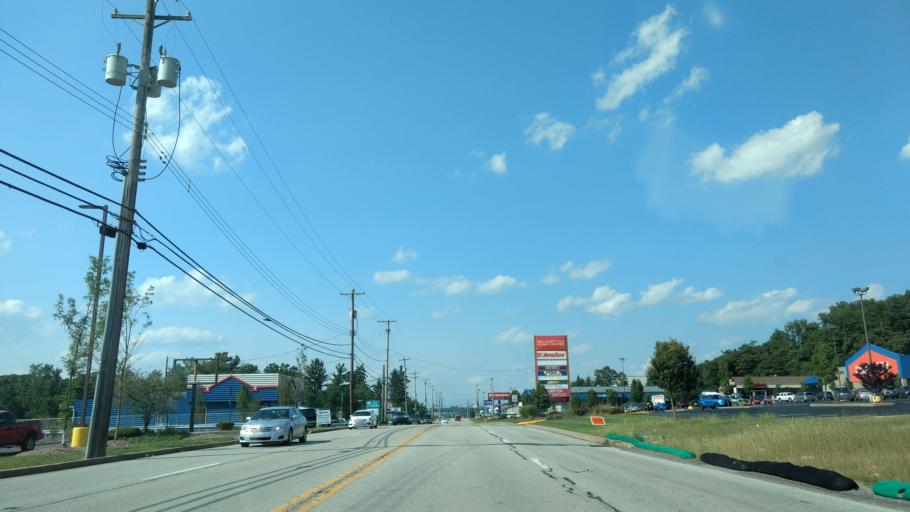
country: US
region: Pennsylvania
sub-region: Allegheny County
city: Allison Park
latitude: 40.5928
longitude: -79.9479
